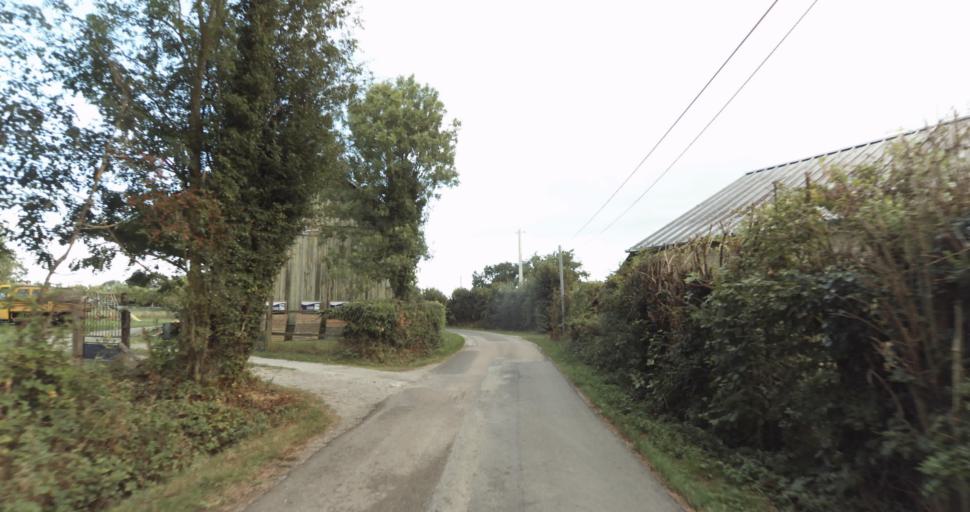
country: FR
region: Lower Normandy
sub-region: Departement de l'Orne
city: Gace
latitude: 48.7683
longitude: 0.3537
